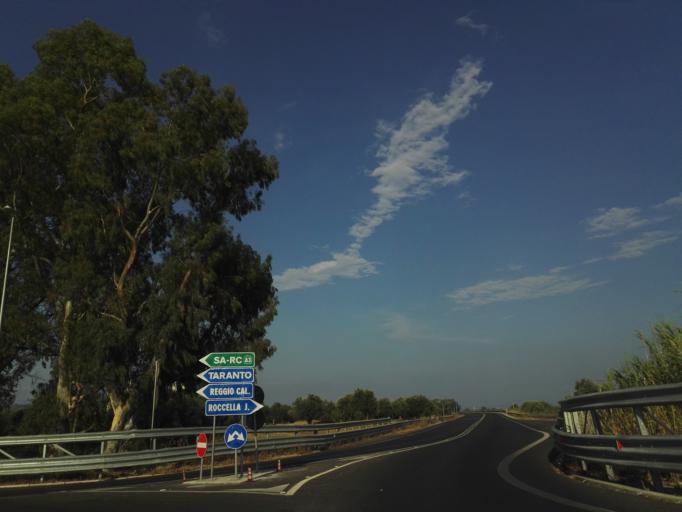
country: IT
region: Calabria
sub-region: Provincia di Reggio Calabria
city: Marina di Gioiosa Ionica
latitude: 38.3062
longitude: 16.3530
